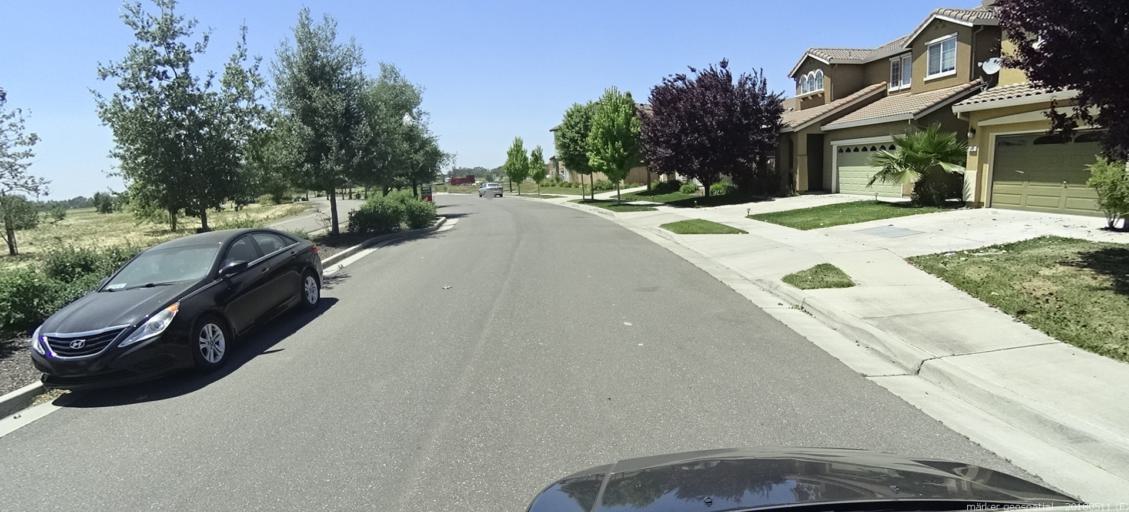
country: US
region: California
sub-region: Yolo County
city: West Sacramento
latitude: 38.6439
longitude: -121.5489
